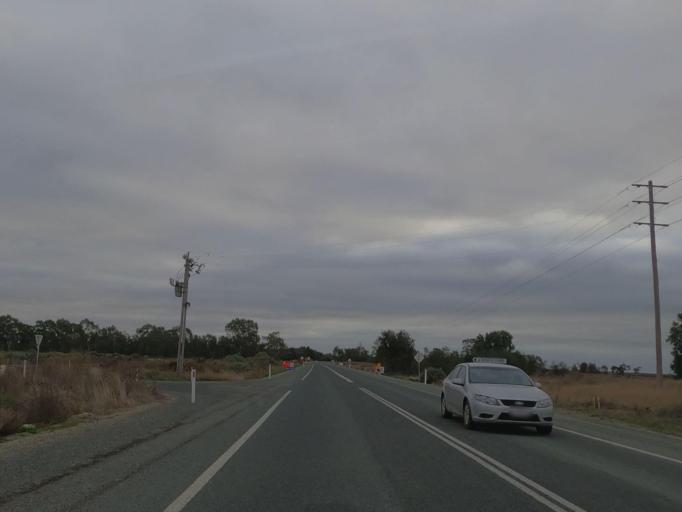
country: AU
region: Victoria
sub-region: Swan Hill
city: Swan Hill
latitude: -35.5382
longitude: 143.7490
